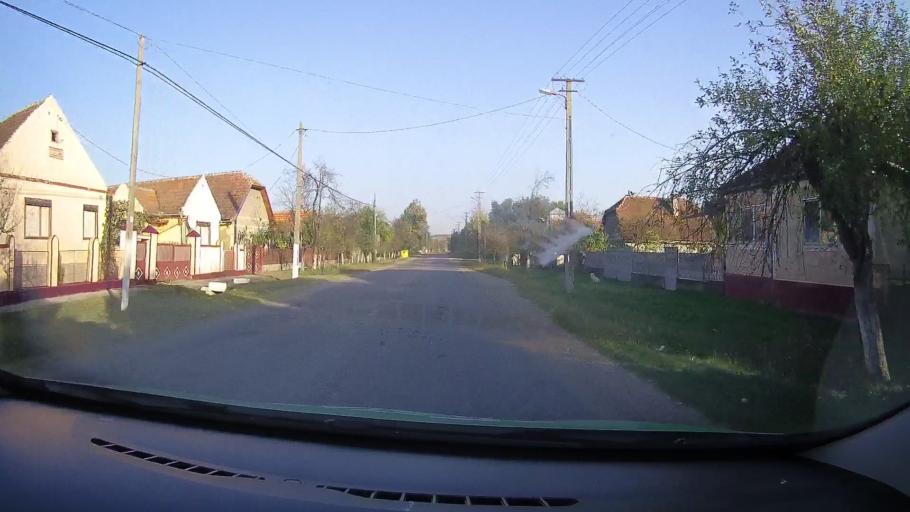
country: RO
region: Arad
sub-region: Comuna Silindia
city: Silindia
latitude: 46.3389
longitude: 21.9194
